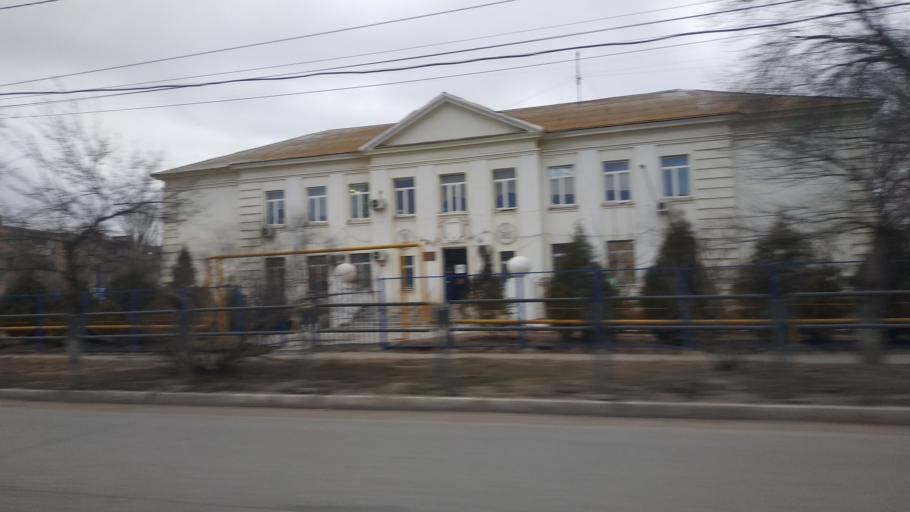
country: RU
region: Astrakhan
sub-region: Gorod Astrakhan'
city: Astrakhan'
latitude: 46.3314
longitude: 48.0111
